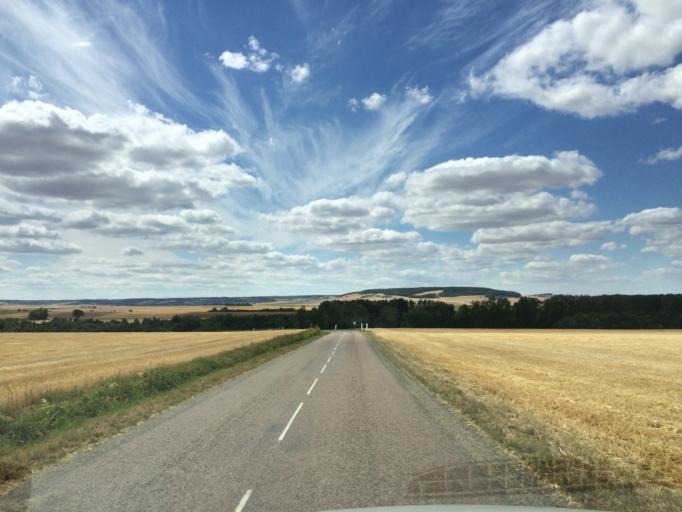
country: FR
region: Bourgogne
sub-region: Departement de l'Yonne
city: Laroche-Saint-Cydroine
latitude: 47.9305
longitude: 3.4491
